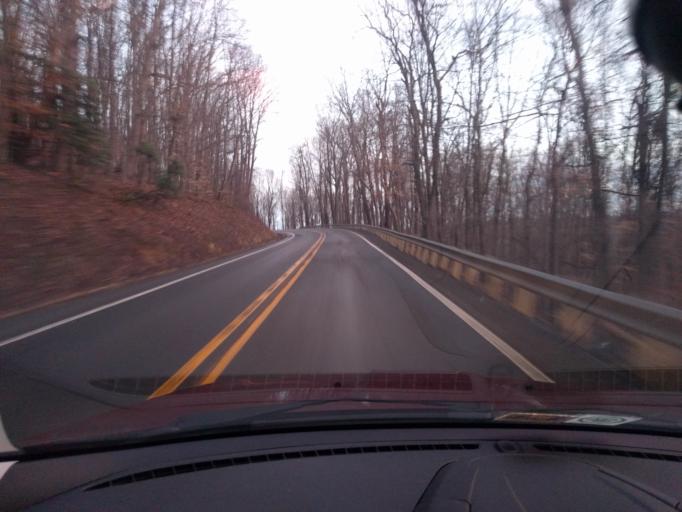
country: US
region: West Virginia
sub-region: Greenbrier County
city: Rainelle
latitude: 37.9904
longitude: -80.8604
